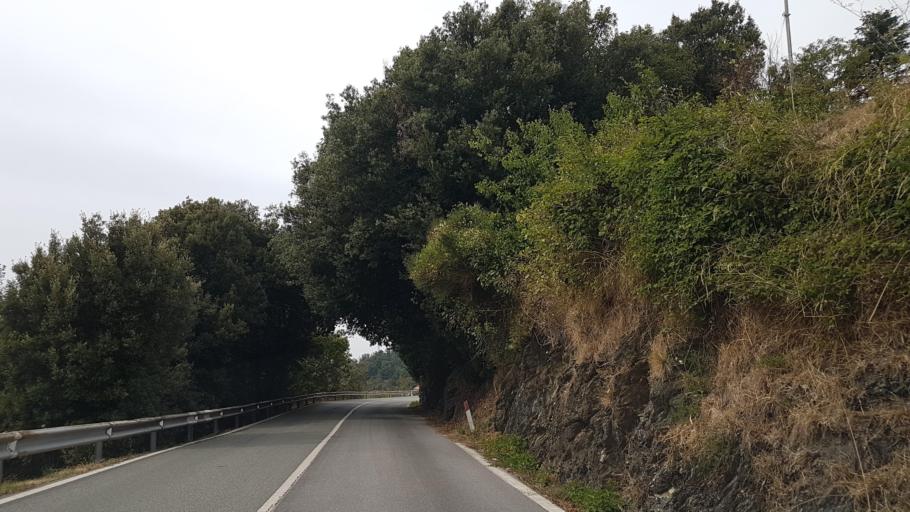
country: IT
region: Liguria
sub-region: Provincia di Genova
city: Castiglione
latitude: 44.2578
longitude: 9.5114
